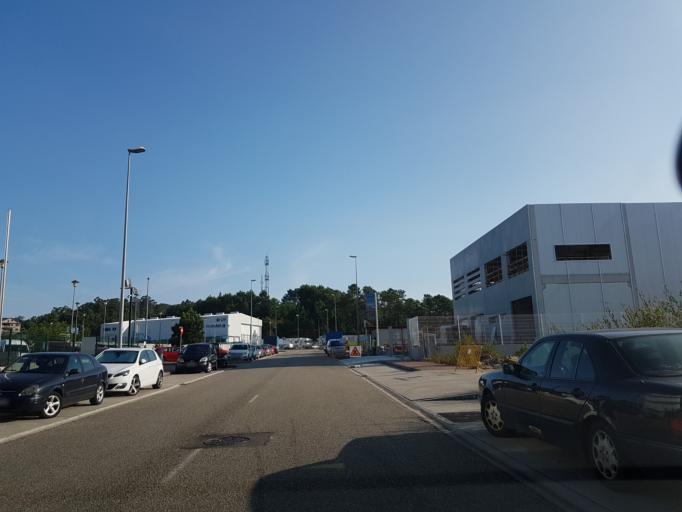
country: ES
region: Galicia
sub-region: Provincia de Pontevedra
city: Porrino
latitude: 42.1880
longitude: -8.6209
